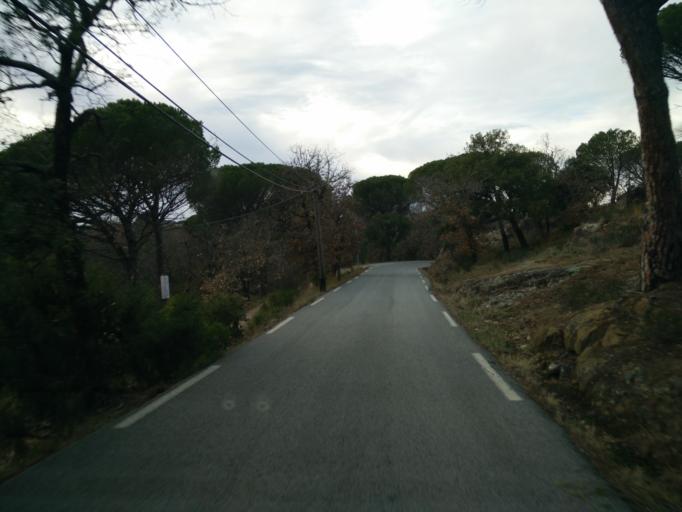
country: FR
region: Provence-Alpes-Cote d'Azur
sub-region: Departement du Var
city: Vidauban
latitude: 43.3945
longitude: 6.4566
